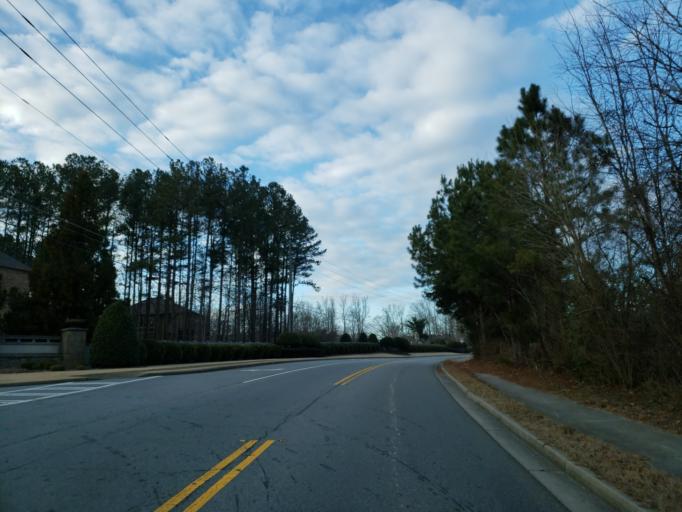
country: US
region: Georgia
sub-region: Cobb County
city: Acworth
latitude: 34.0065
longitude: -84.6793
